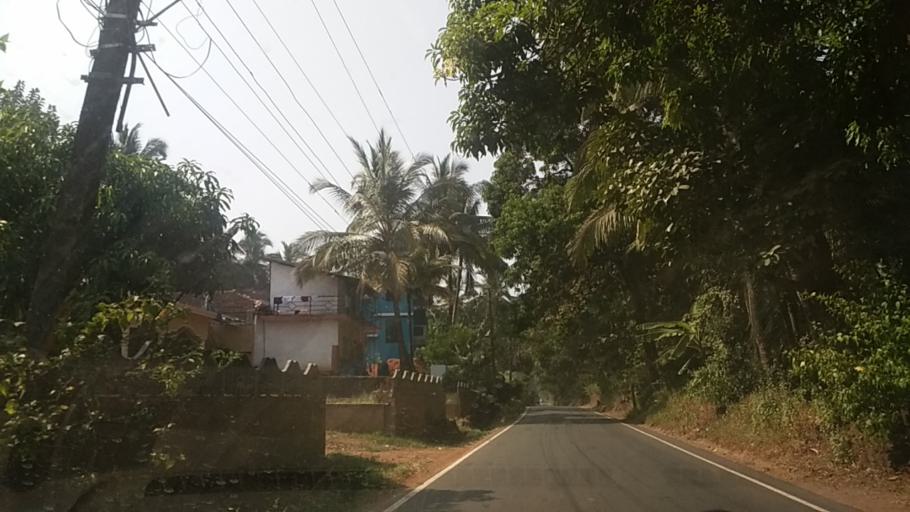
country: IN
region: Goa
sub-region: North Goa
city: Queula
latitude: 15.3852
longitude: 73.9505
